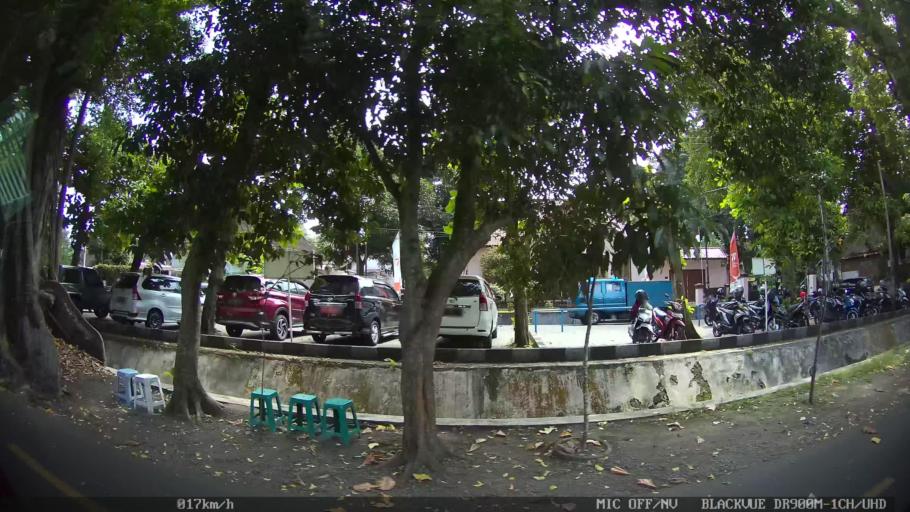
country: ID
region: Daerah Istimewa Yogyakarta
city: Yogyakarta
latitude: -7.7870
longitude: 110.3840
